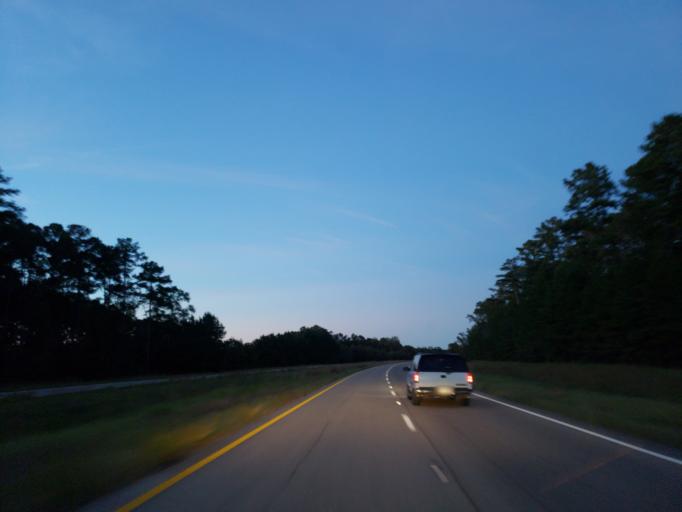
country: US
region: Mississippi
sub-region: Clarke County
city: Quitman
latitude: 31.8598
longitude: -88.7202
